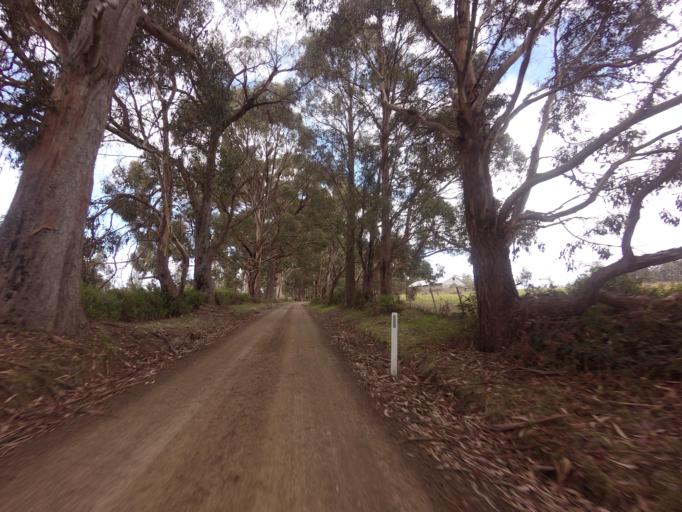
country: AU
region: Tasmania
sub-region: Huon Valley
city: Cygnet
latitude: -43.4095
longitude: 147.0188
